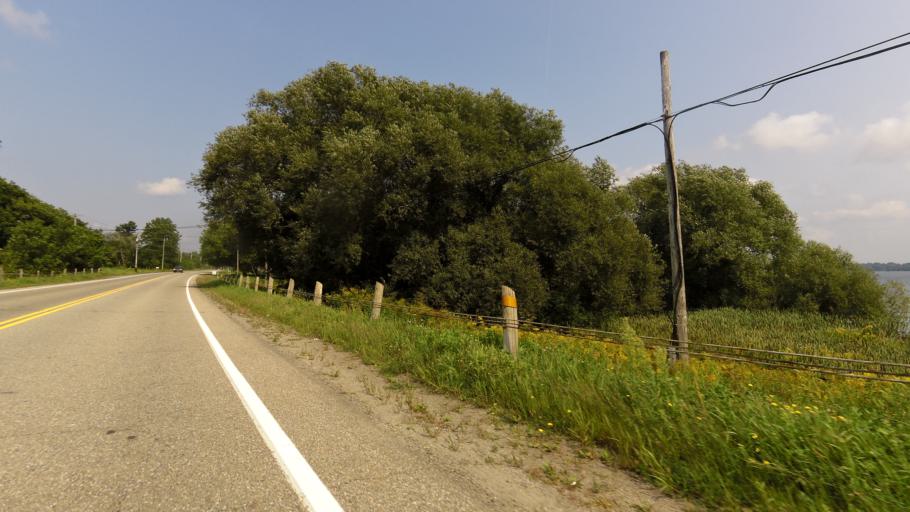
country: CA
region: Ontario
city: Prescott
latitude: 44.6738
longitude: -75.5661
